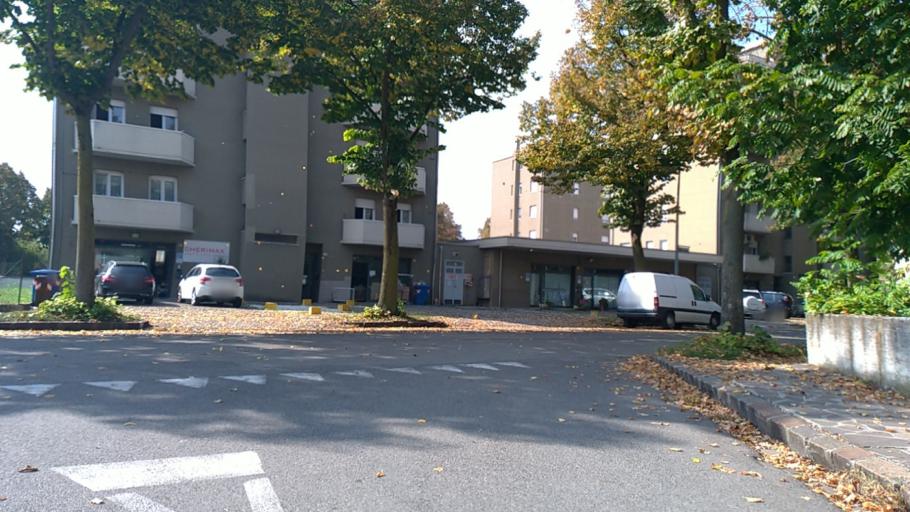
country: IT
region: Emilia-Romagna
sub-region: Provincia di Modena
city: Carpi Centro
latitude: 44.7721
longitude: 10.8719
